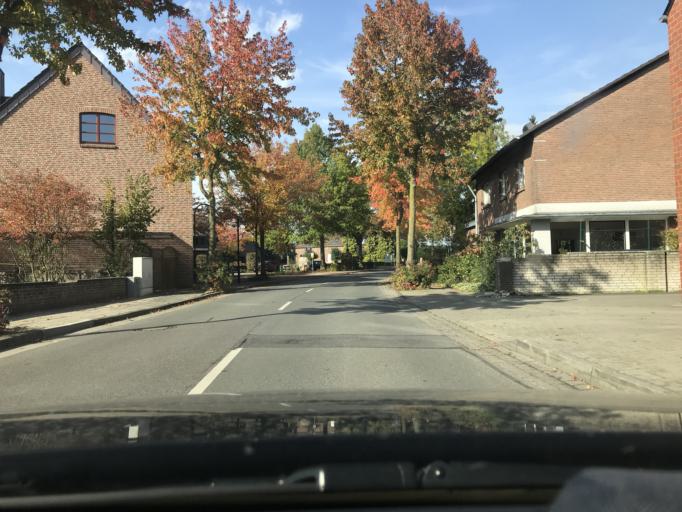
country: DE
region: North Rhine-Westphalia
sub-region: Regierungsbezirk Dusseldorf
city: Uedem
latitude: 51.6899
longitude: 6.2673
